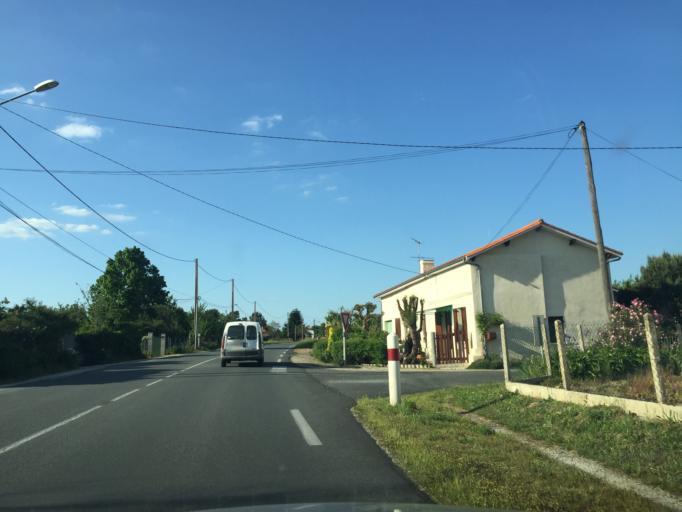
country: FR
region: Poitou-Charentes
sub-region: Departement de la Charente-Maritime
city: Saint-Aigulin
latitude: 45.1192
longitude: -0.0100
